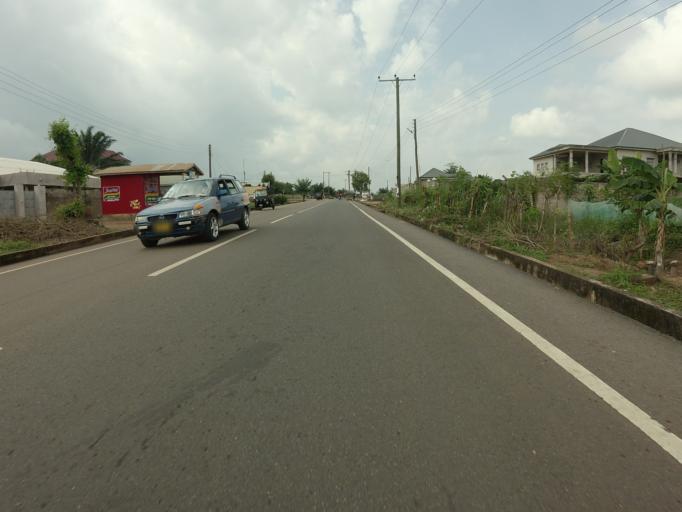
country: GH
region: Volta
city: Ho
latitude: 6.6275
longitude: 0.4881
